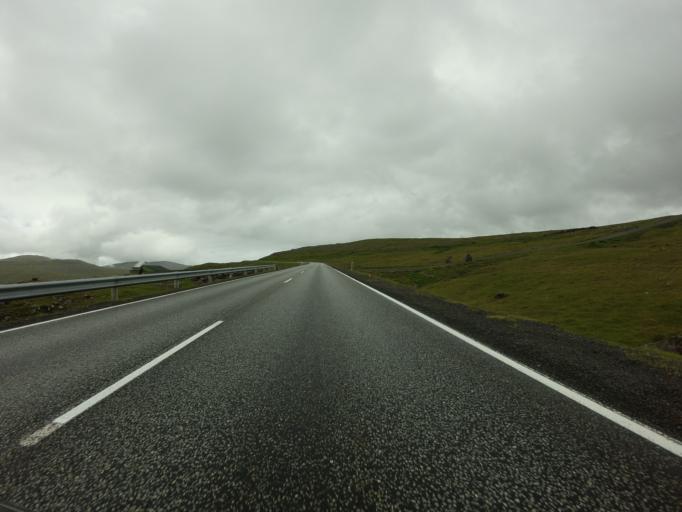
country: FO
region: Streymoy
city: Vestmanna
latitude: 62.1231
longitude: -7.1376
